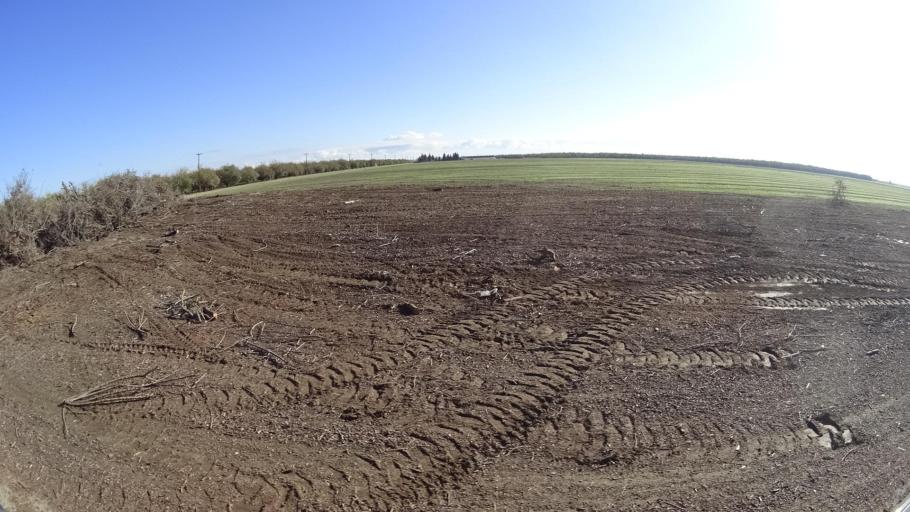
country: US
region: California
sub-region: Kern County
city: McFarland
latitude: 35.6809
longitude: -119.2676
